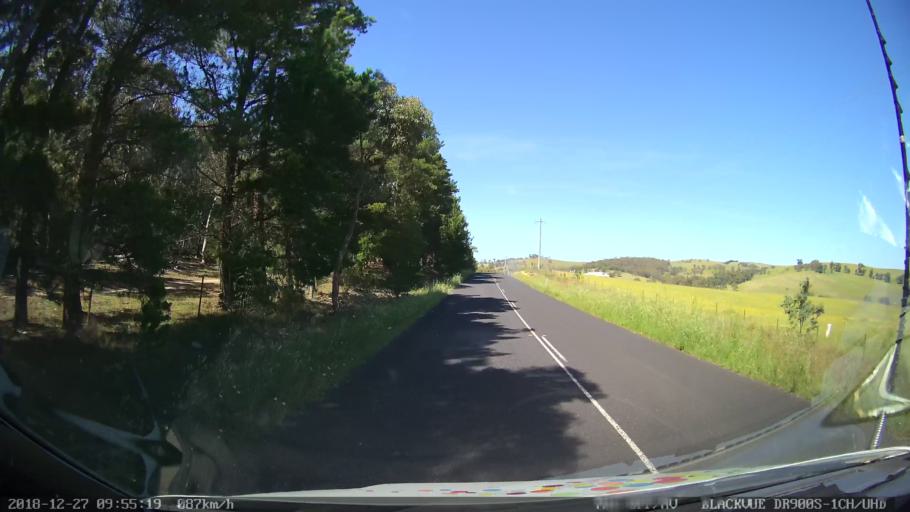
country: AU
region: New South Wales
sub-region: Lithgow
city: Portland
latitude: -33.4005
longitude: 149.9770
